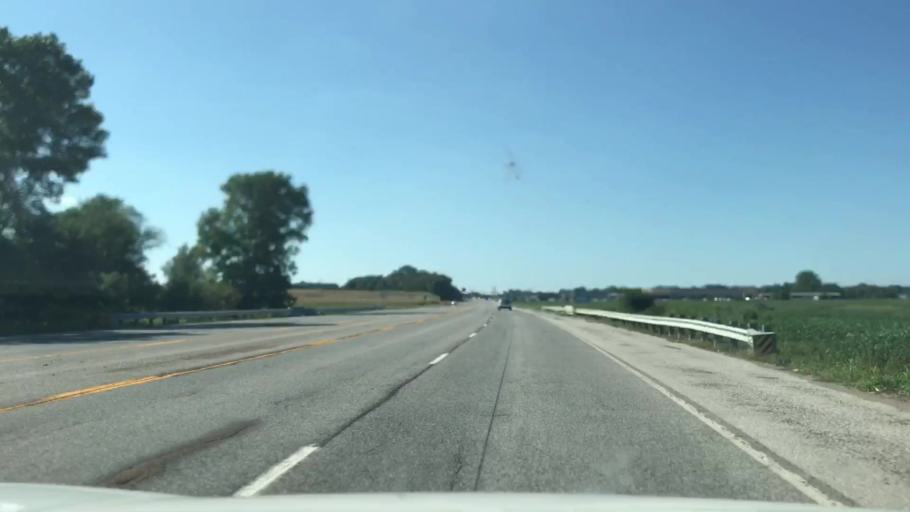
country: US
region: Illinois
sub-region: Madison County
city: Roxana
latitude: 38.8534
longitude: -90.0577
